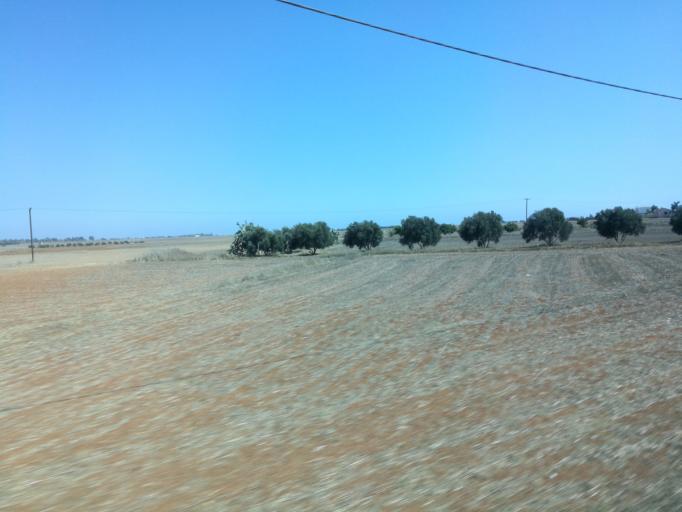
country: CY
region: Larnaka
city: Xylotymbou
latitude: 35.0317
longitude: 33.7574
